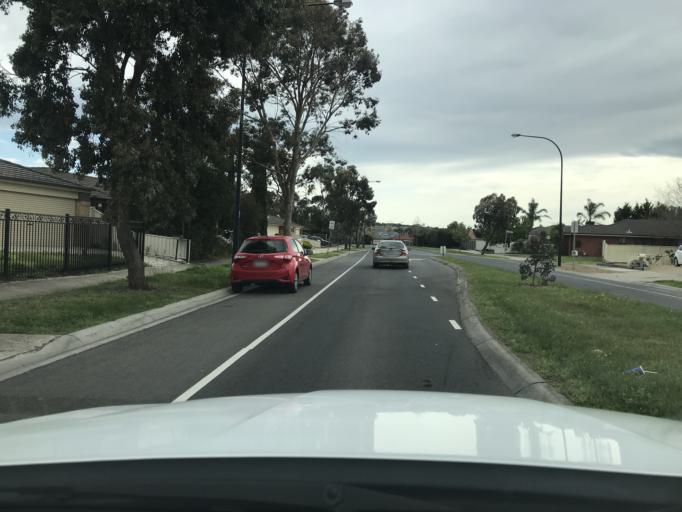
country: AU
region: Victoria
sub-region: Hume
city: Craigieburn
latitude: -37.5892
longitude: 144.9368
